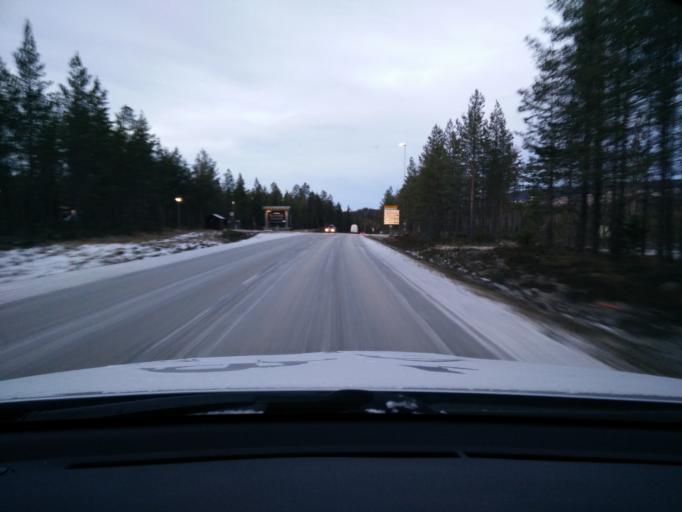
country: SE
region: Jaemtland
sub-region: Bergs Kommun
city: Hoverberg
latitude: 62.5050
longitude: 14.1990
